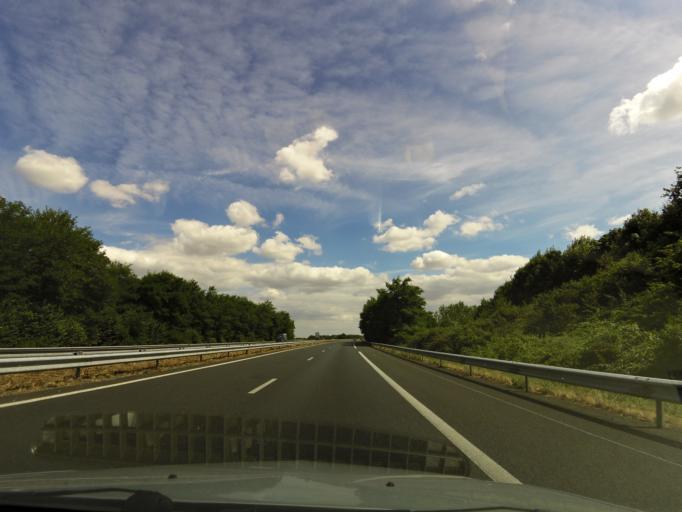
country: FR
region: Pays de la Loire
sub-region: Departement de la Vendee
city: Chauche
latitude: 46.8417
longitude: -1.2423
